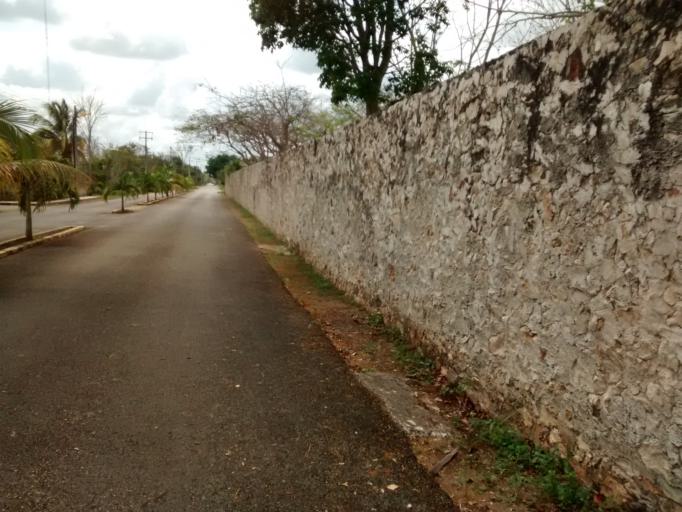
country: MX
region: Yucatan
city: Valladolid
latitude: 20.6854
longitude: -88.1834
